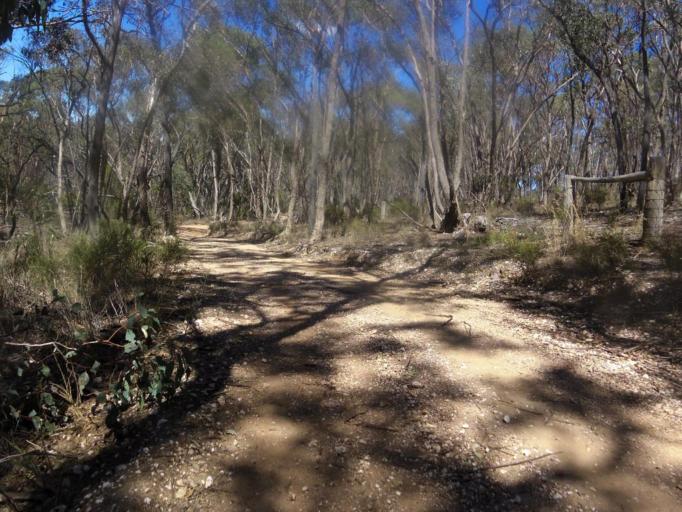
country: AU
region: Victoria
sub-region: Mount Alexander
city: Castlemaine
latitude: -37.0568
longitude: 144.1897
